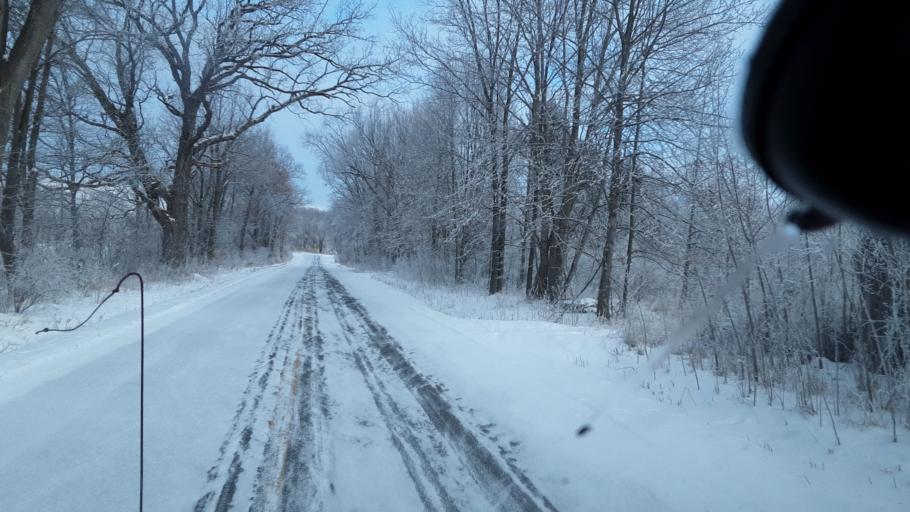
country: US
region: Michigan
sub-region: Ingham County
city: Leslie
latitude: 42.4194
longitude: -84.4823
